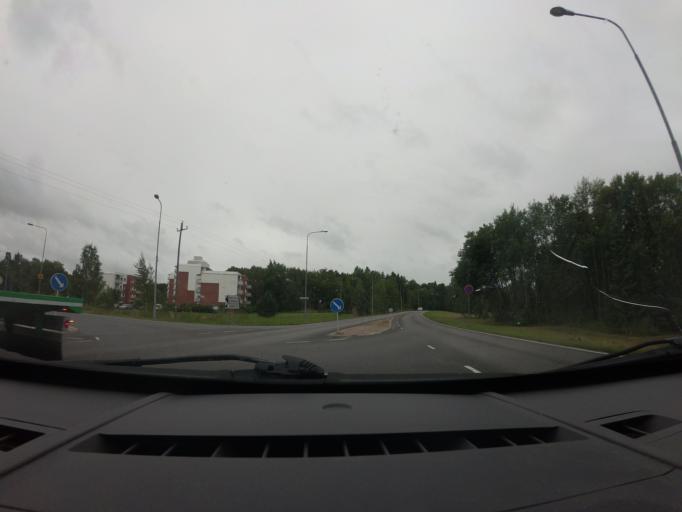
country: FI
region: Varsinais-Suomi
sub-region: Turku
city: Turku
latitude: 60.4208
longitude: 22.3003
